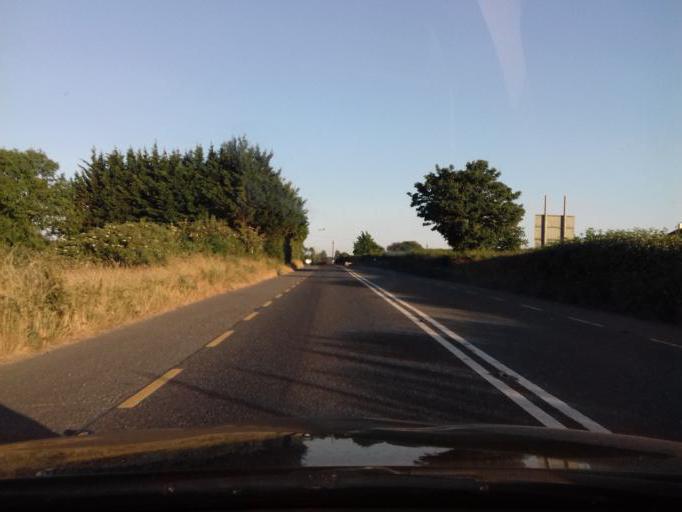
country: IE
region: Leinster
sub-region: Fingal County
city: Blanchardstown
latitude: 53.4427
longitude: -6.3400
